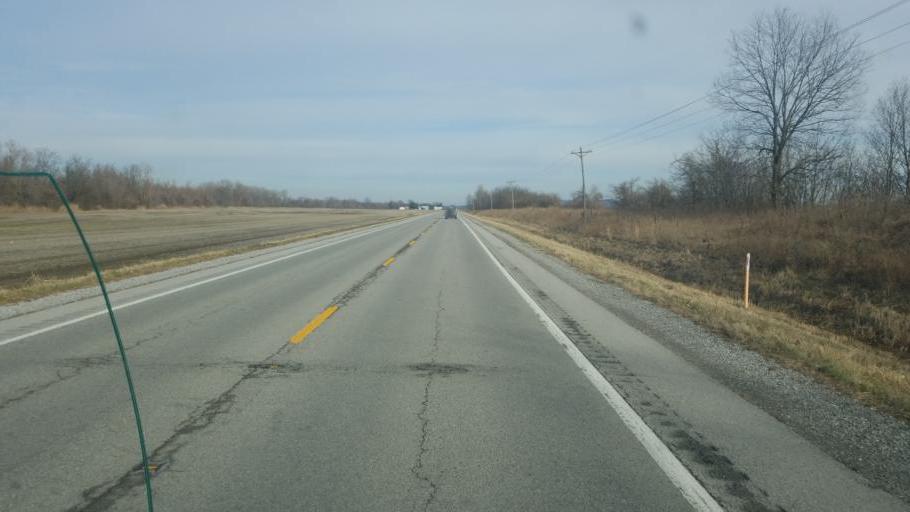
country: US
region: Missouri
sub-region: Cape Girardeau County
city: Cape Girardeau
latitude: 37.3356
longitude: -89.4093
